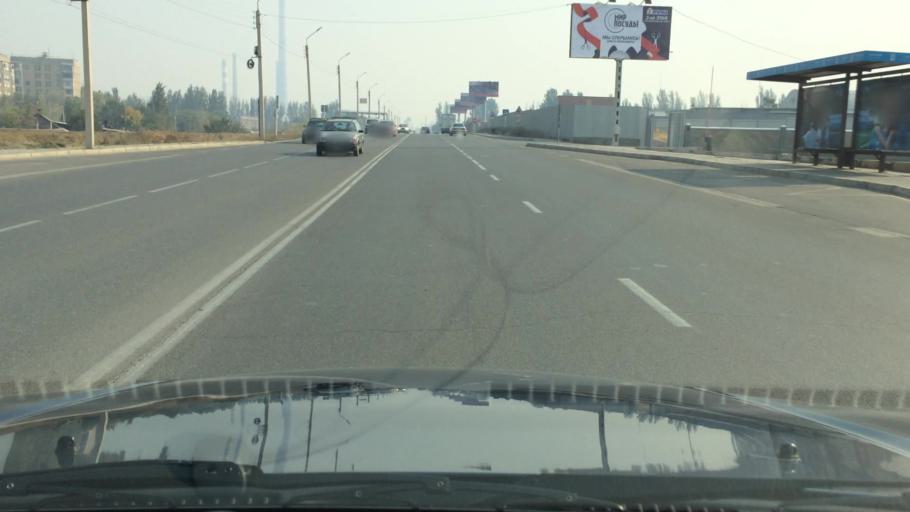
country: KG
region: Chuy
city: Bishkek
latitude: 42.8660
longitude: 74.6319
